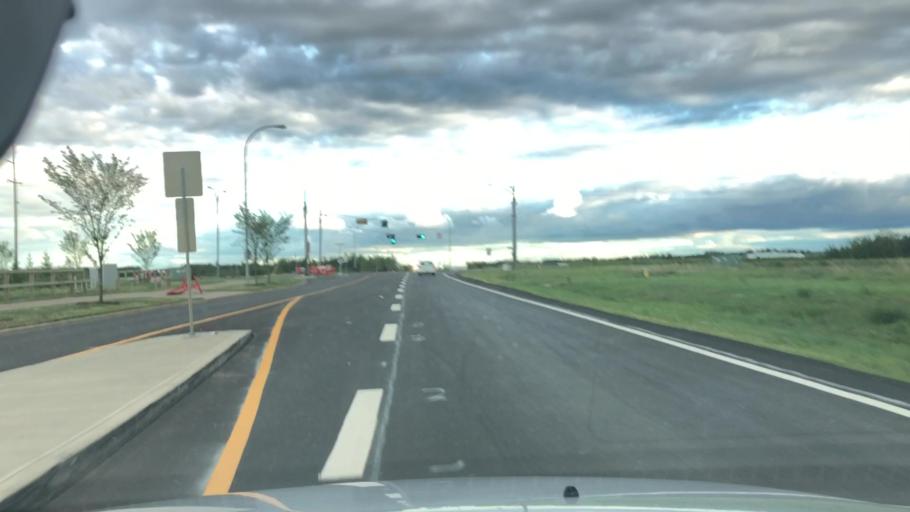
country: CA
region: Alberta
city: St. Albert
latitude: 53.6156
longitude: -113.5698
